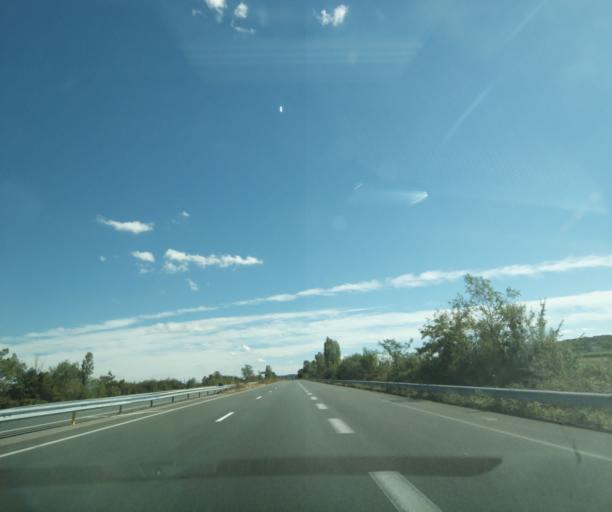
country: FR
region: Aquitaine
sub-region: Departement du Lot-et-Garonne
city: Buzet-sur-Baise
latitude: 44.2484
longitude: 0.3037
